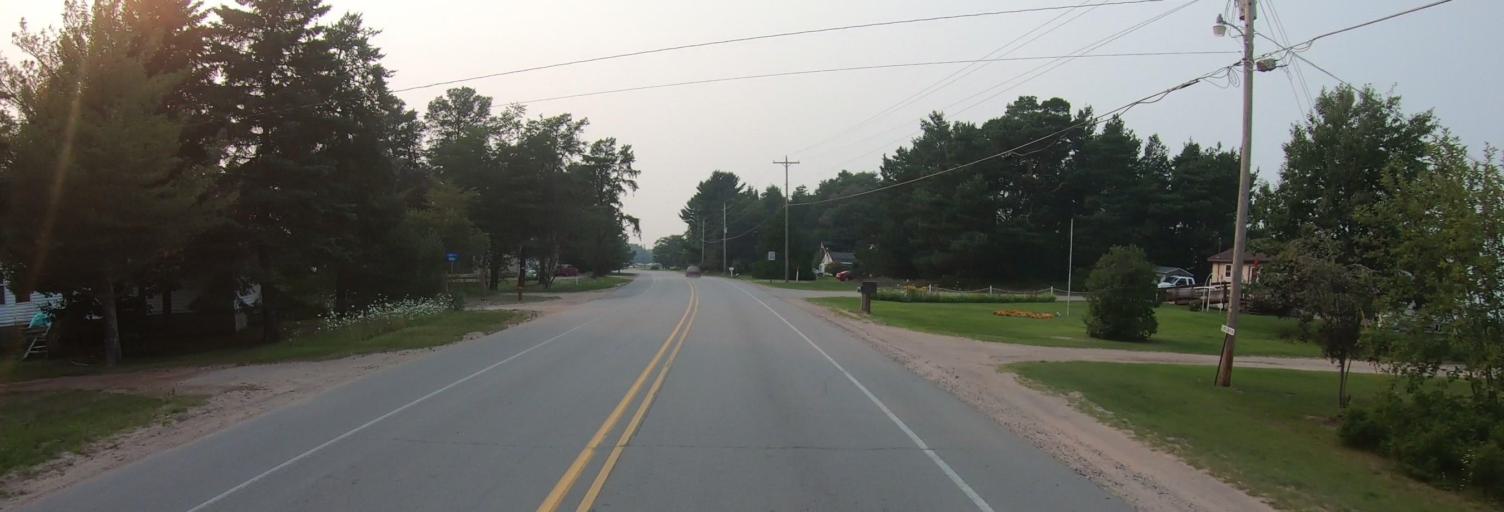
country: US
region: Michigan
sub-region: Chippewa County
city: Sault Ste. Marie
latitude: 46.4520
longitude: -84.6025
